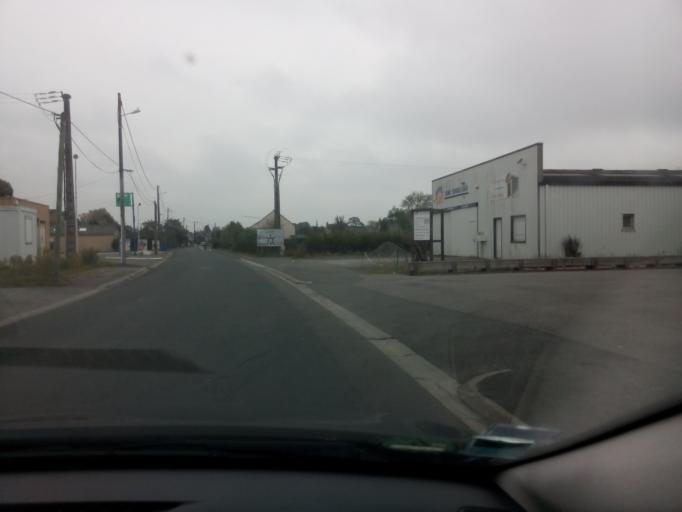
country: FR
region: Pays de la Loire
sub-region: Departement de Maine-et-Loire
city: Tierce
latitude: 47.6195
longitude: -0.5163
